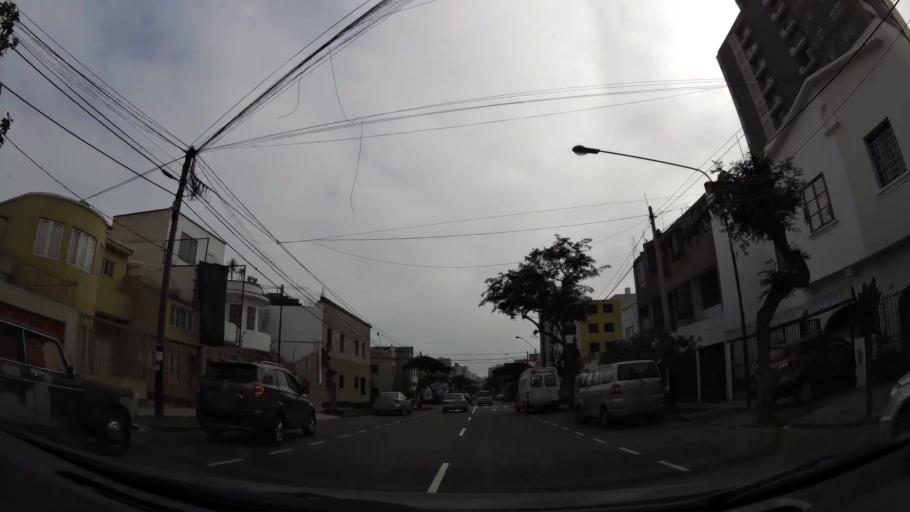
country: PE
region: Lima
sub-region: Lima
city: San Isidro
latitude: -12.0835
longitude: -77.0423
